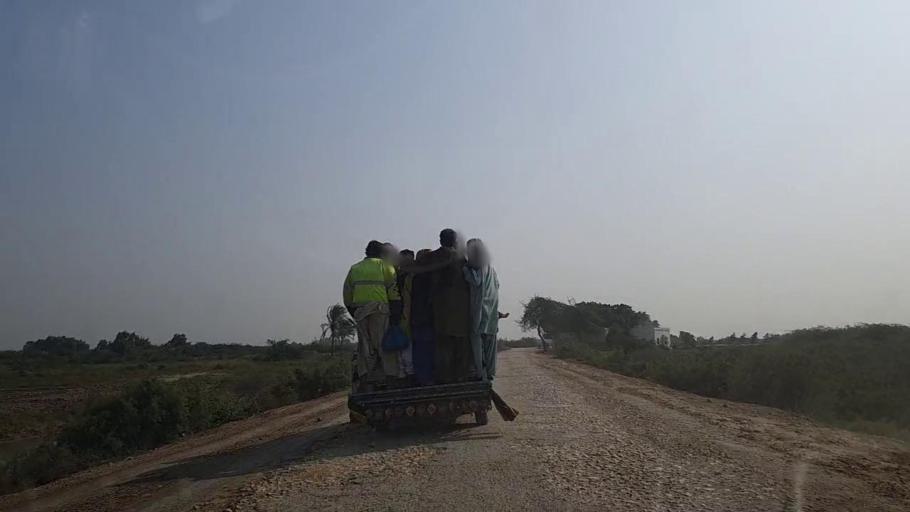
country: PK
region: Sindh
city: Keti Bandar
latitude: 24.2453
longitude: 67.6353
